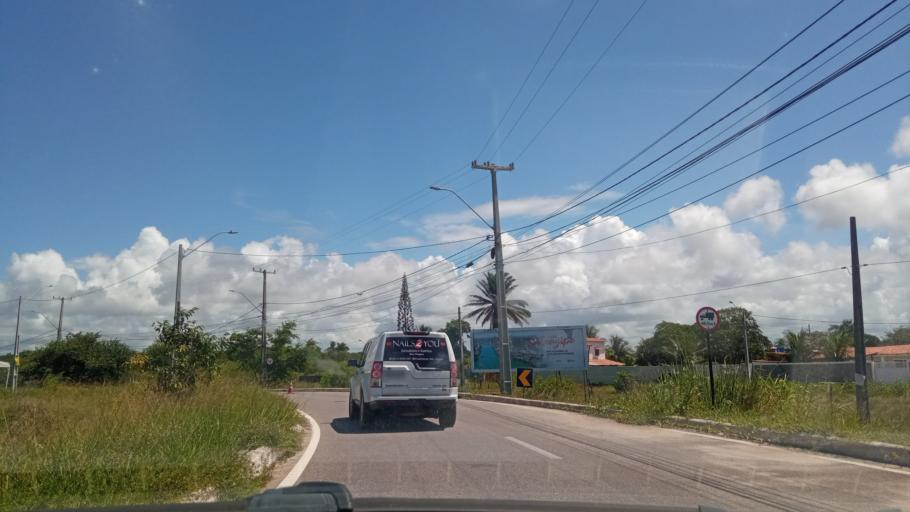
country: BR
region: Pernambuco
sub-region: Jaboatao Dos Guararapes
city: Jaboatao
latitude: -8.2371
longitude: -34.9402
